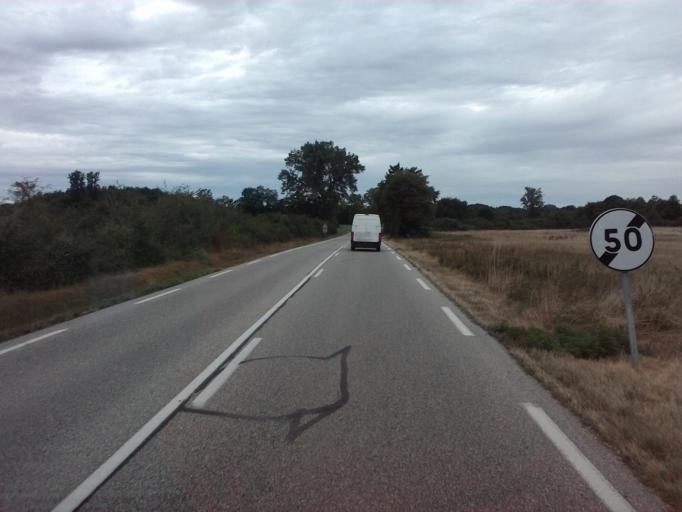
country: FR
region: Rhone-Alpes
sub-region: Departement de l'Isere
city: Sermerieu
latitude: 45.7194
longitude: 5.4177
